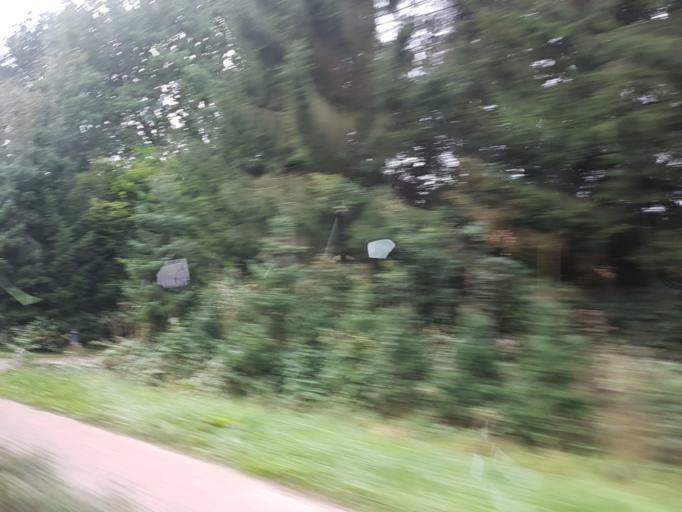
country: BE
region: Flanders
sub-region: Provincie Antwerpen
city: Zandhoven
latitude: 51.2096
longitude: 4.6269
